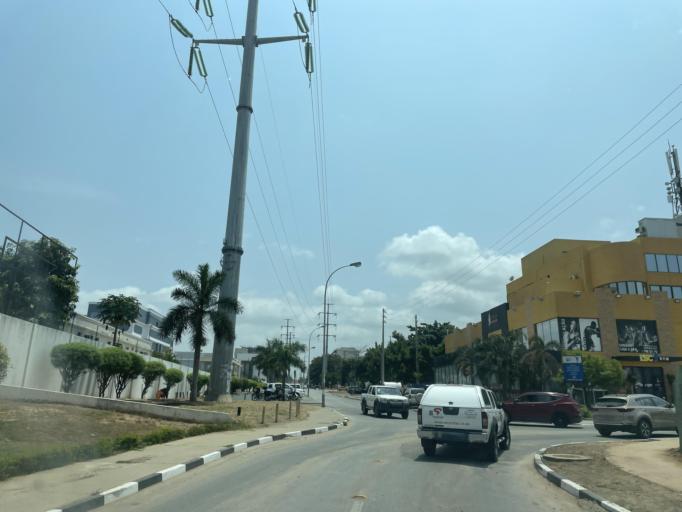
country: AO
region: Luanda
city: Luanda
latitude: -8.9073
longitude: 13.1951
